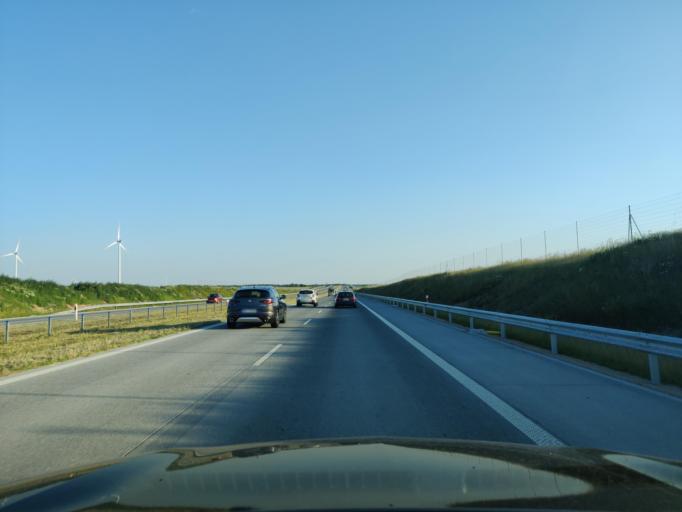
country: PL
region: Masovian Voivodeship
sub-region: Powiat mlawski
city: Wisniewo
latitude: 53.0594
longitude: 20.3645
